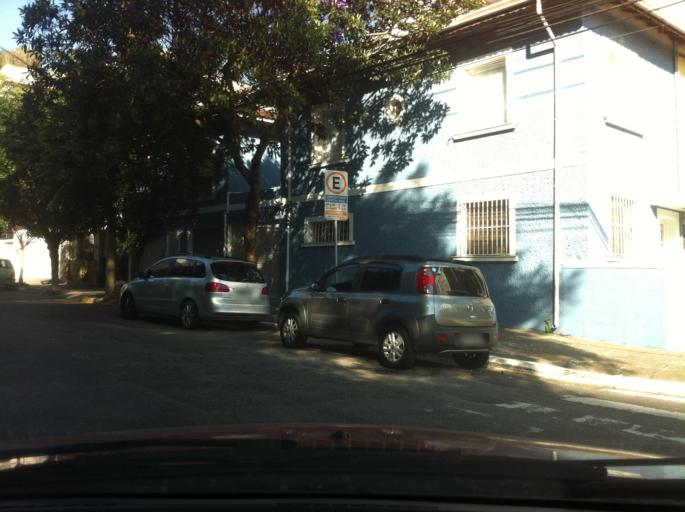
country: BR
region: Sao Paulo
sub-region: Sao Paulo
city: Sao Paulo
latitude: -23.5953
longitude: -46.6491
